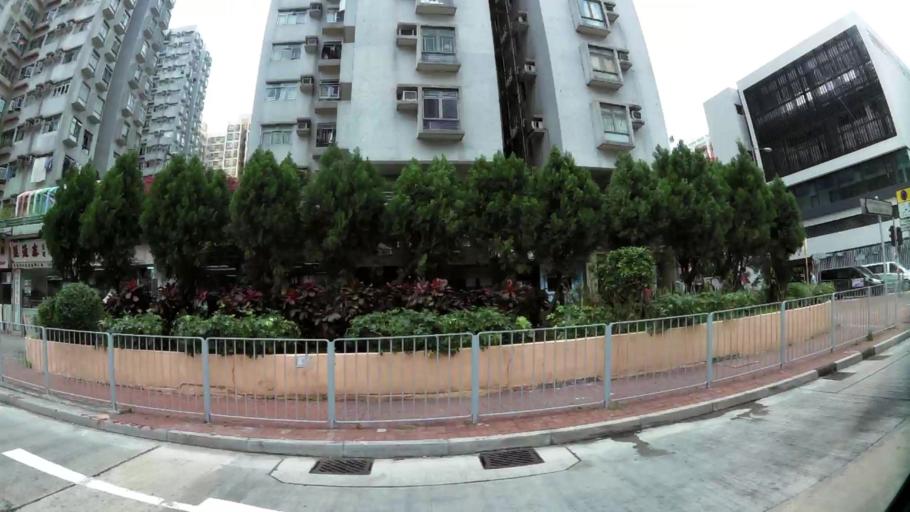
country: HK
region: Tuen Mun
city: Tuen Mun
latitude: 22.3864
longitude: 113.9809
